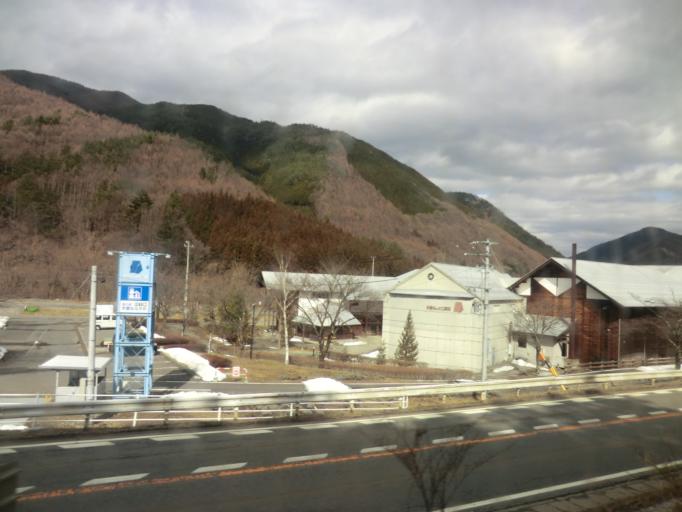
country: JP
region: Nagano
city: Tatsuno
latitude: 35.9855
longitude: 137.8416
